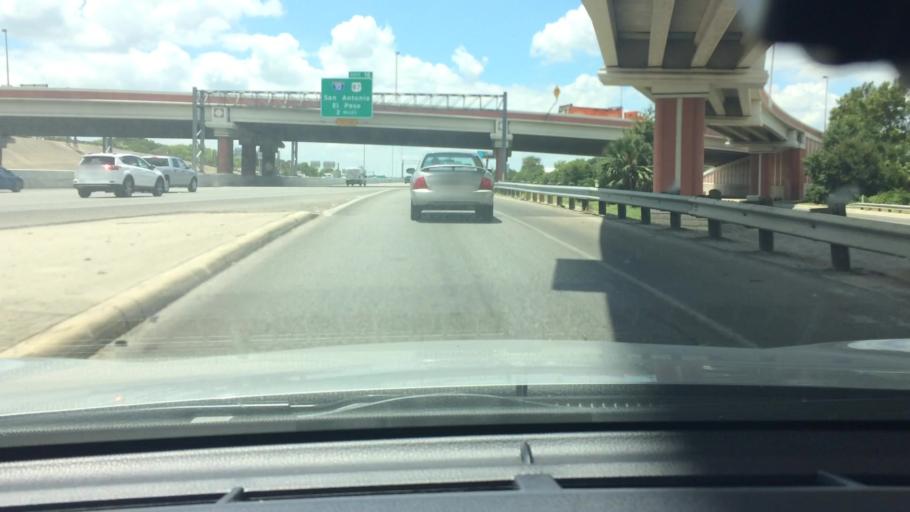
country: US
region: Texas
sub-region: Bexar County
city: Castle Hills
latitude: 29.5210
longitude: -98.5117
